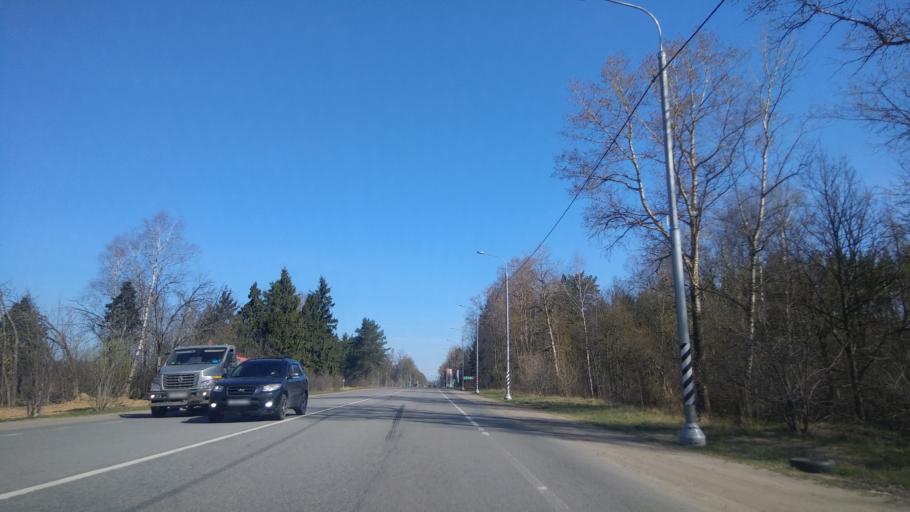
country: RU
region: Moskovskaya
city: Pushkino
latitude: 56.0276
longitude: 37.8711
